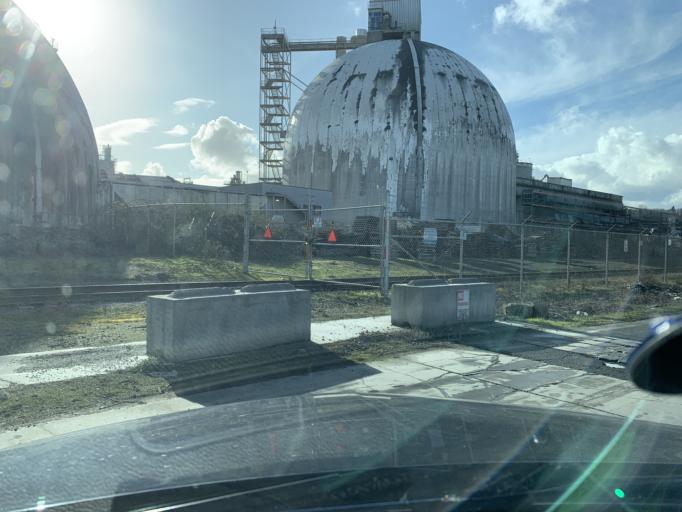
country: US
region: Washington
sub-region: King County
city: Seattle
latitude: 47.5693
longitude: -122.3416
